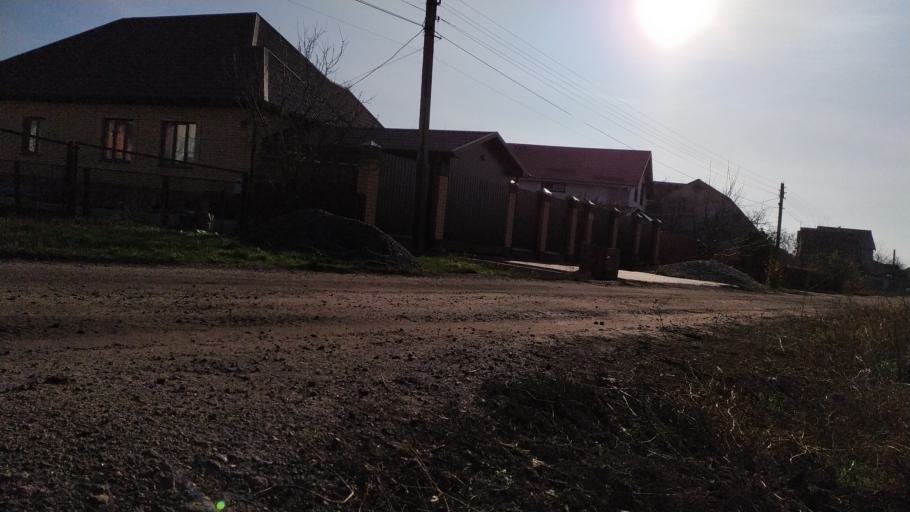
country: RU
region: Kursk
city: Kursk
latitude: 51.6434
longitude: 36.1320
